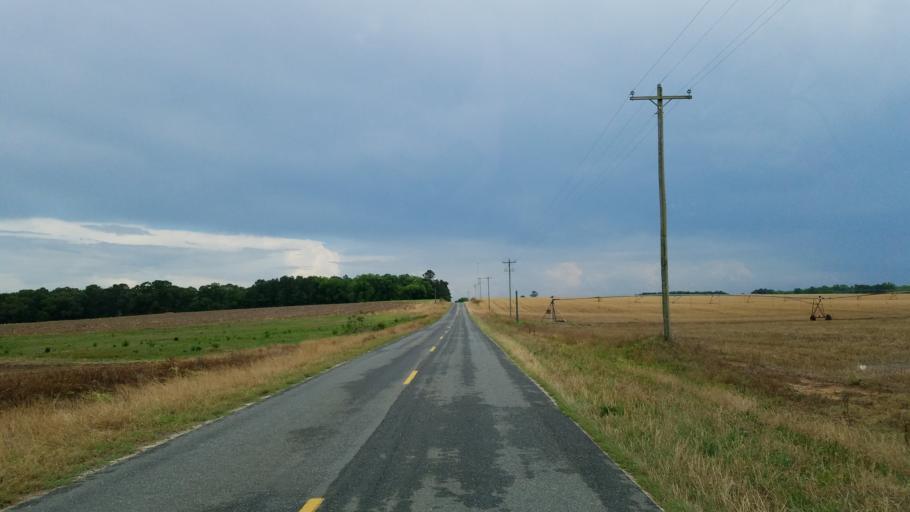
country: US
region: Georgia
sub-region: Dooly County
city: Unadilla
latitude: 32.2559
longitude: -83.7971
